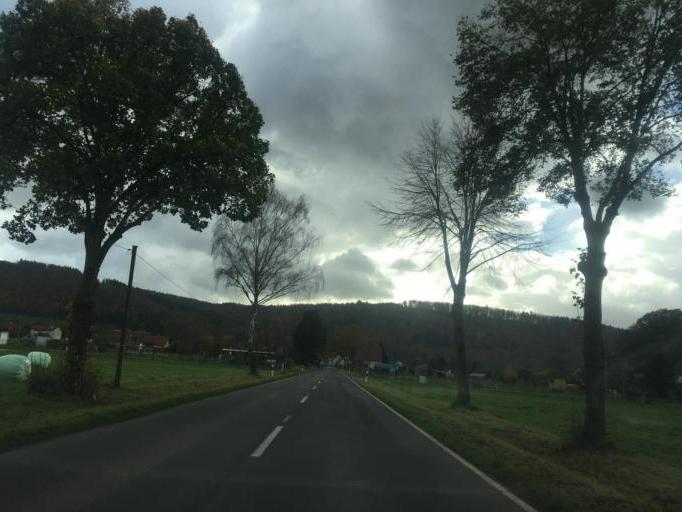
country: DE
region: Lower Saxony
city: Bodenfelde
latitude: 51.6347
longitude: 9.5230
